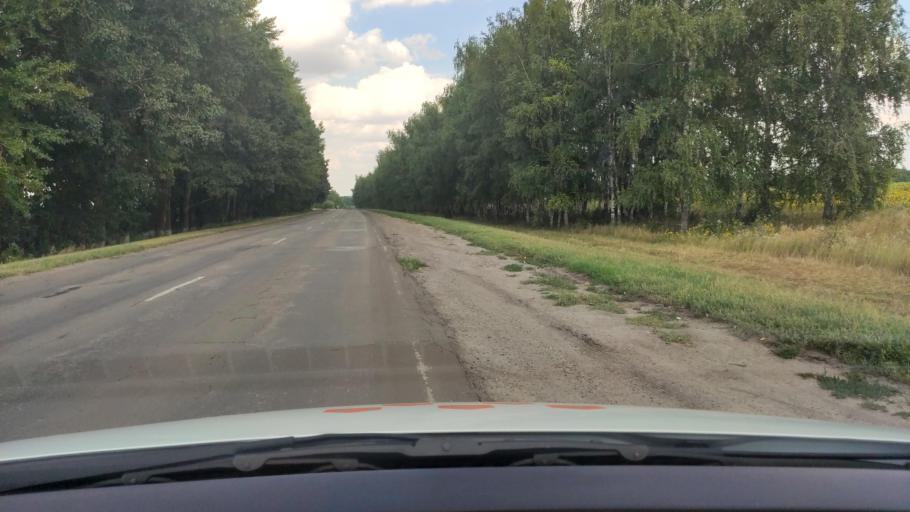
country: RU
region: Voronezj
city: Panino
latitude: 51.6602
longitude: 40.1471
